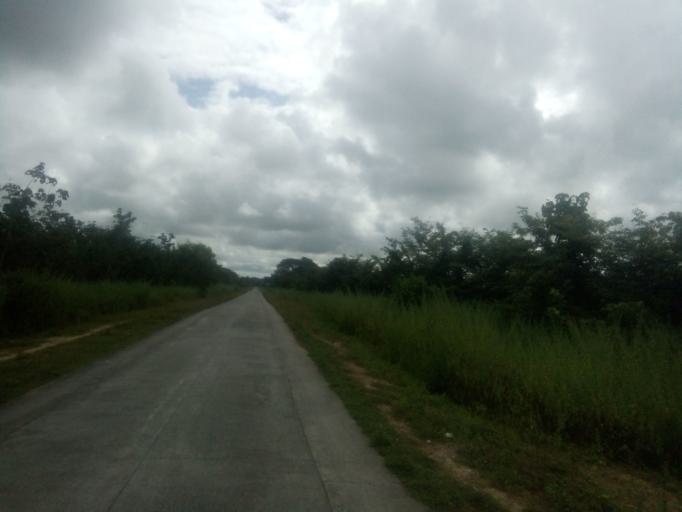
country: MM
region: Bago
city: Nyaunglebin
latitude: 17.9216
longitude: 96.4951
